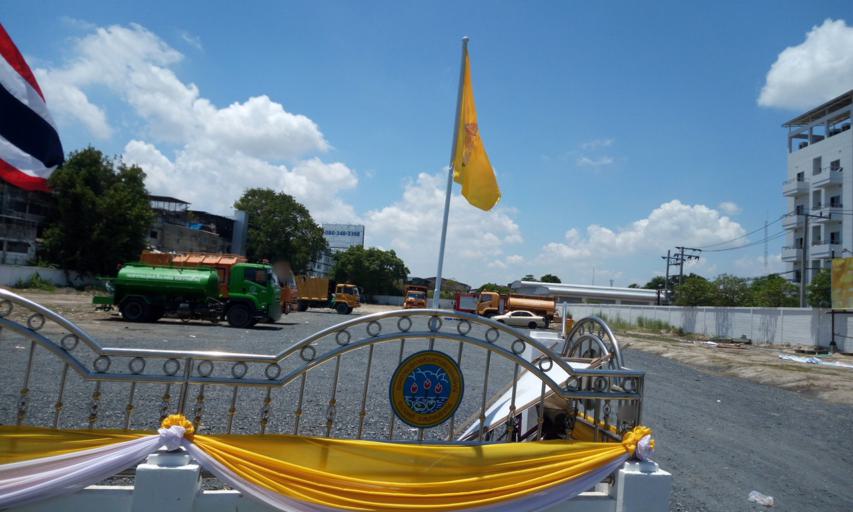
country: TH
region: Bangkok
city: Bang Na
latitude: 13.6093
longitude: 100.7020
